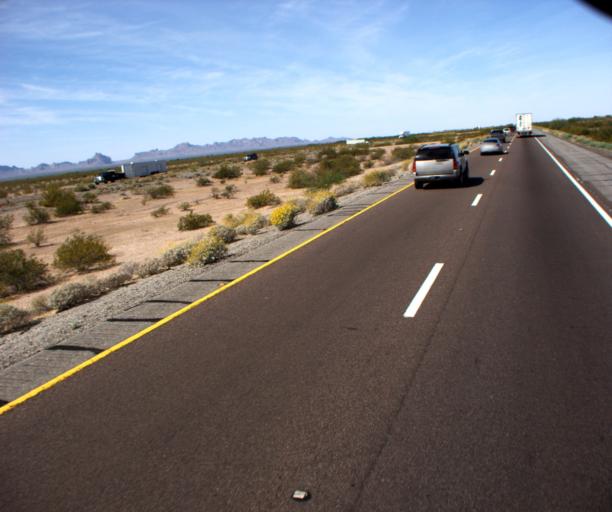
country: US
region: Arizona
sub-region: La Paz County
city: Salome
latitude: 33.5436
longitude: -113.1839
